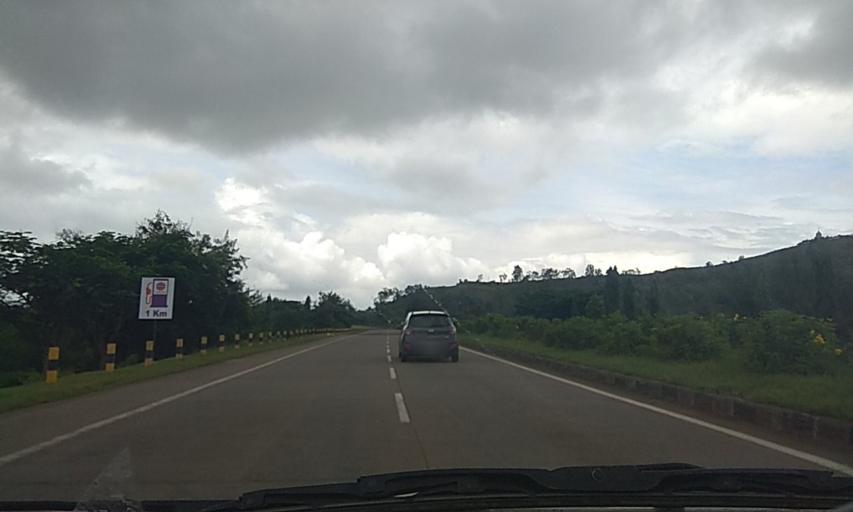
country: IN
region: Karnataka
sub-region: Belgaum
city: Sankeshwar
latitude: 16.2840
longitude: 74.4455
